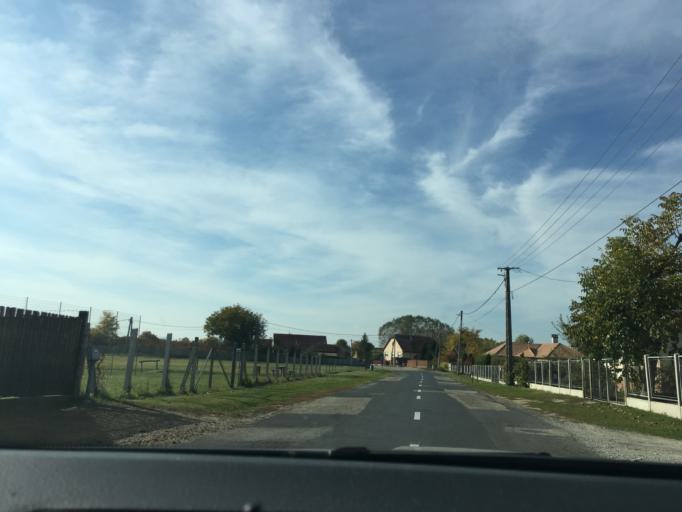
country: HU
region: Hajdu-Bihar
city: Nyirabrany
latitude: 47.5321
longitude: 21.9926
